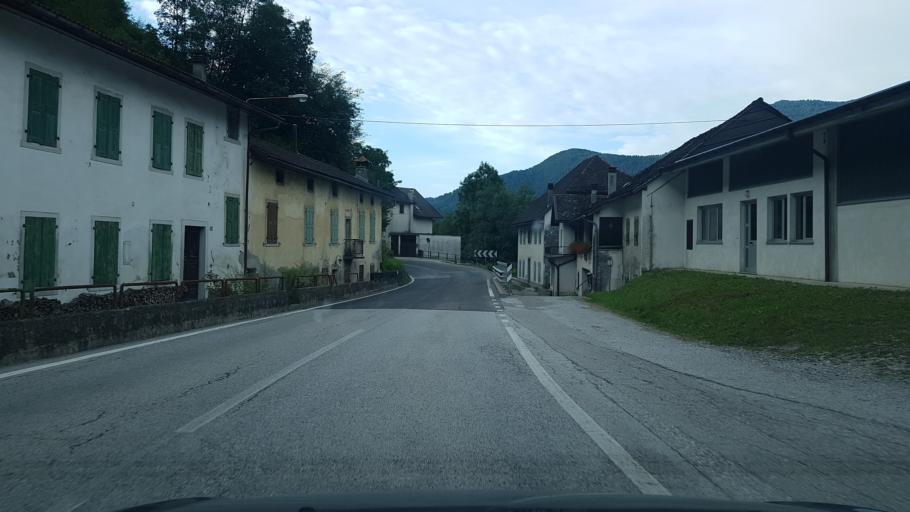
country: IT
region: Friuli Venezia Giulia
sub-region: Provincia di Udine
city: Comeglians
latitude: 46.5005
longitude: 12.8653
